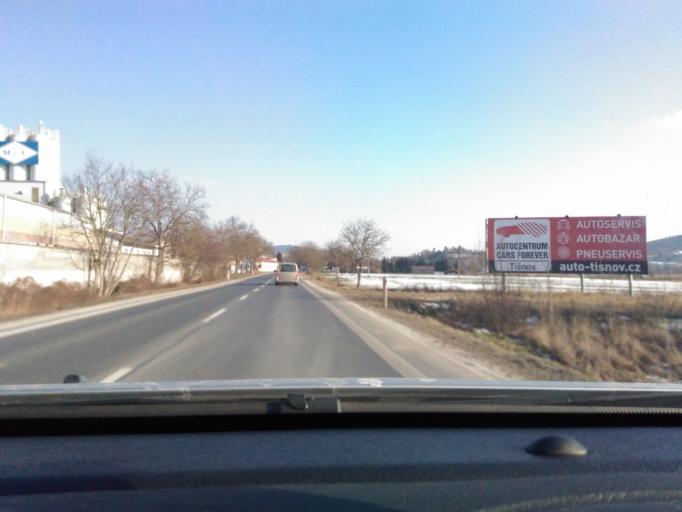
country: CZ
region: South Moravian
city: Tisnov
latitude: 49.3372
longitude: 16.4309
